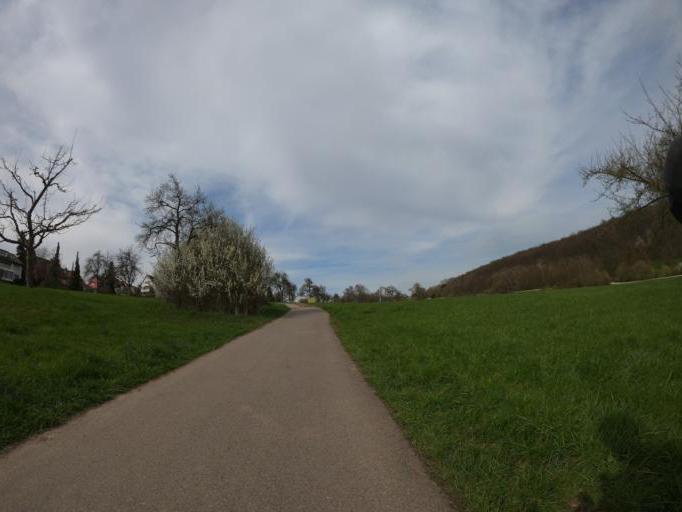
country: DE
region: Baden-Wuerttemberg
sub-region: Regierungsbezirk Stuttgart
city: Ostfildern
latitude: 48.7170
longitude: 9.2366
